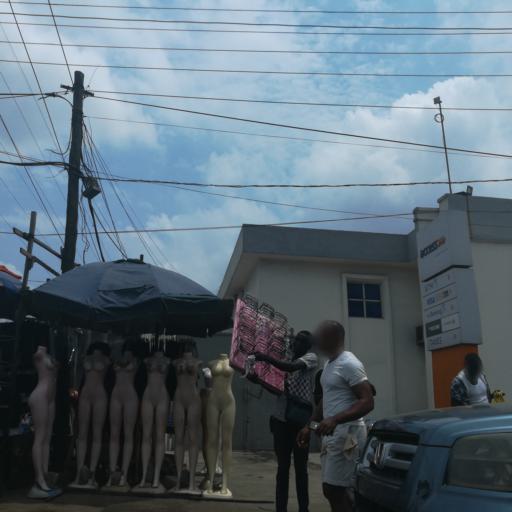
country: NG
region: Lagos
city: Ojota
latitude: 6.5881
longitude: 3.3805
